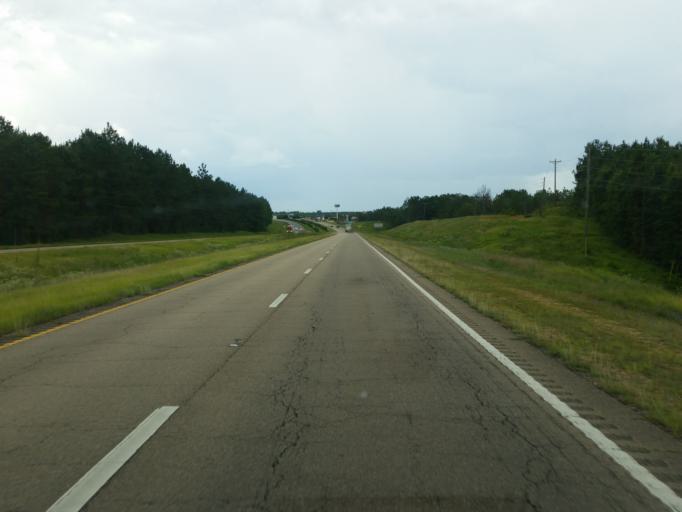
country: US
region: Mississippi
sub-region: George County
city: Lucedale
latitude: 30.9542
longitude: -88.6079
